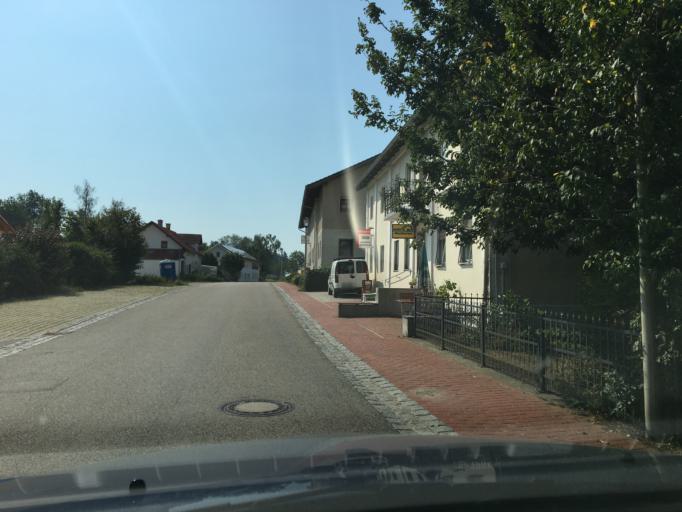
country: DE
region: Bavaria
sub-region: Upper Bavaria
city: Niederbergkirchen
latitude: 48.2991
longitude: 12.4853
